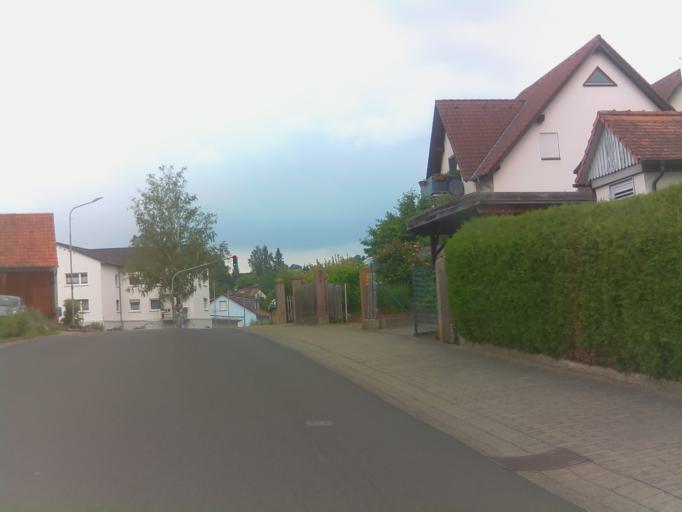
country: DE
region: Hesse
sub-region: Regierungsbezirk Giessen
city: Schlitz
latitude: 50.6732
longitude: 9.5571
